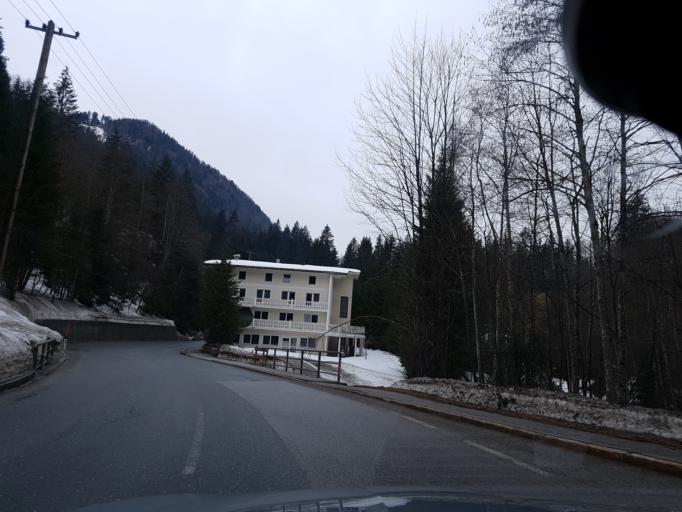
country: AT
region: Tyrol
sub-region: Politischer Bezirk Kufstein
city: Worgl
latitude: 47.4673
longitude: 12.0860
